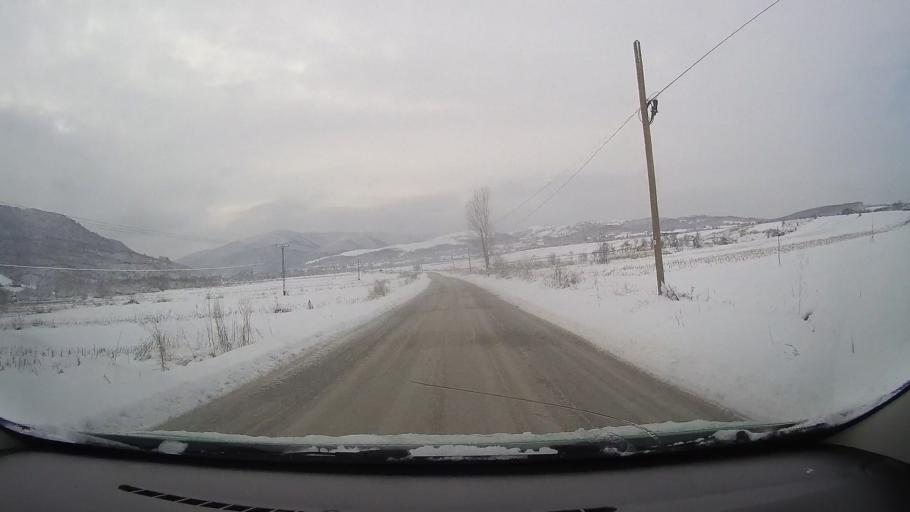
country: RO
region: Alba
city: Pianu de Sus
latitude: 45.9145
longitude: 23.4826
